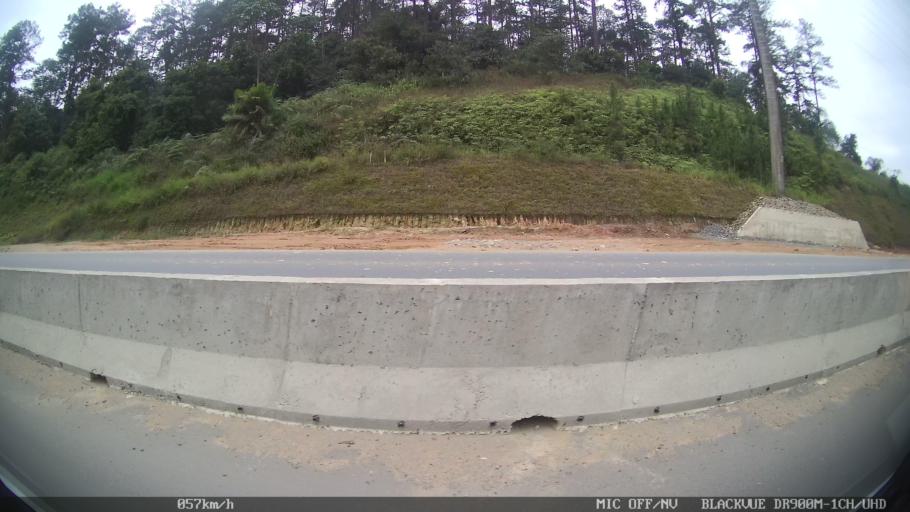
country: BR
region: Santa Catarina
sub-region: Joinville
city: Joinville
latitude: -26.2567
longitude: -48.8966
